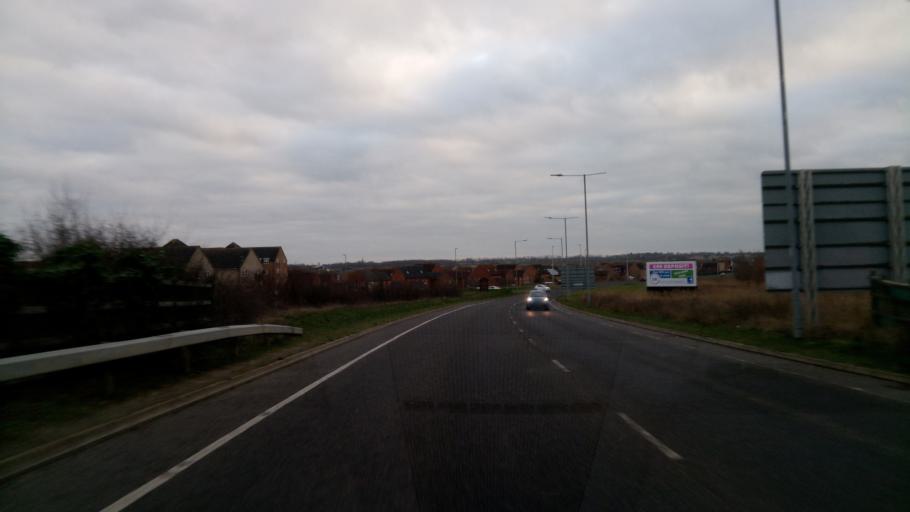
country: GB
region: England
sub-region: Cambridgeshire
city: Yaxley
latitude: 52.5399
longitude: -0.2812
